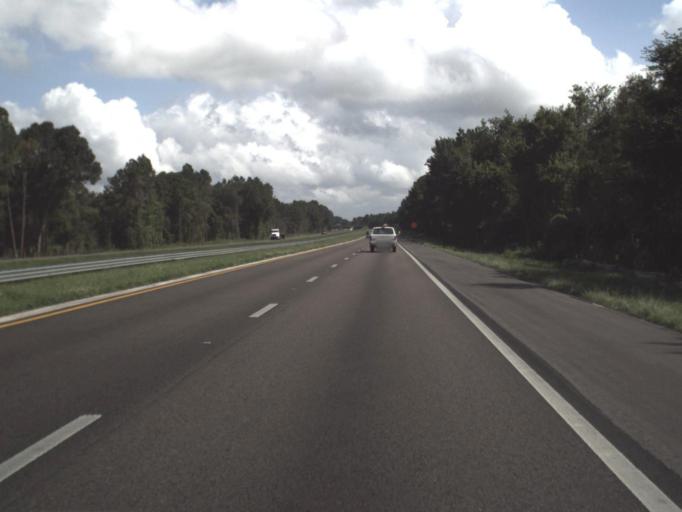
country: US
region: Florida
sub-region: Pasco County
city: San Antonio
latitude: 28.3446
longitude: -82.3221
